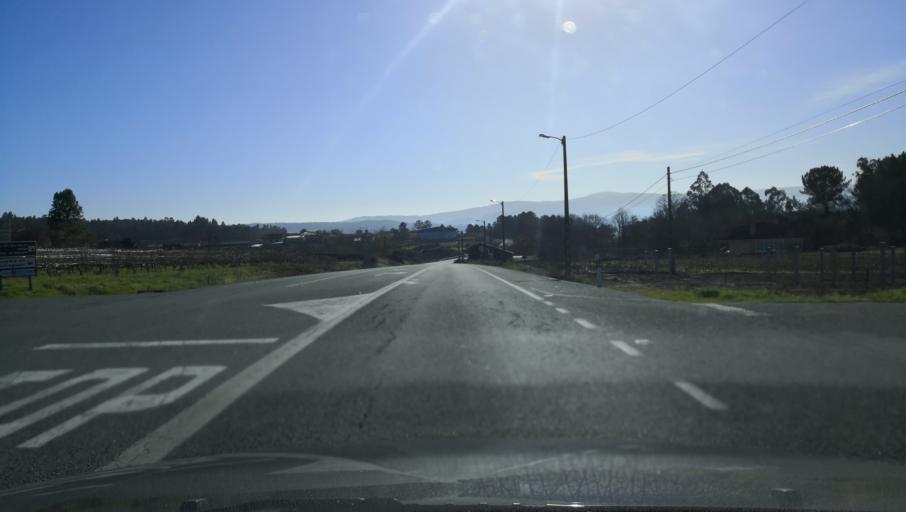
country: ES
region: Galicia
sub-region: Provincia da Coruna
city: Ribeira
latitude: 42.7845
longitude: -8.4378
